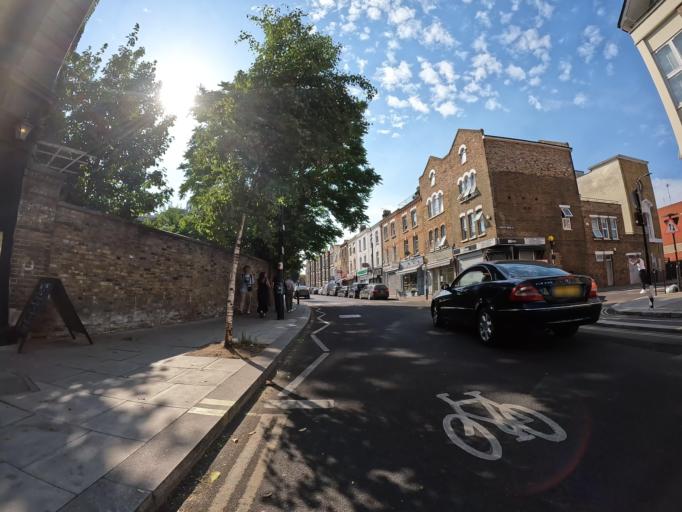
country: GB
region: England
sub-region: Greater London
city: Hendon
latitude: 51.5805
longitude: -0.2082
